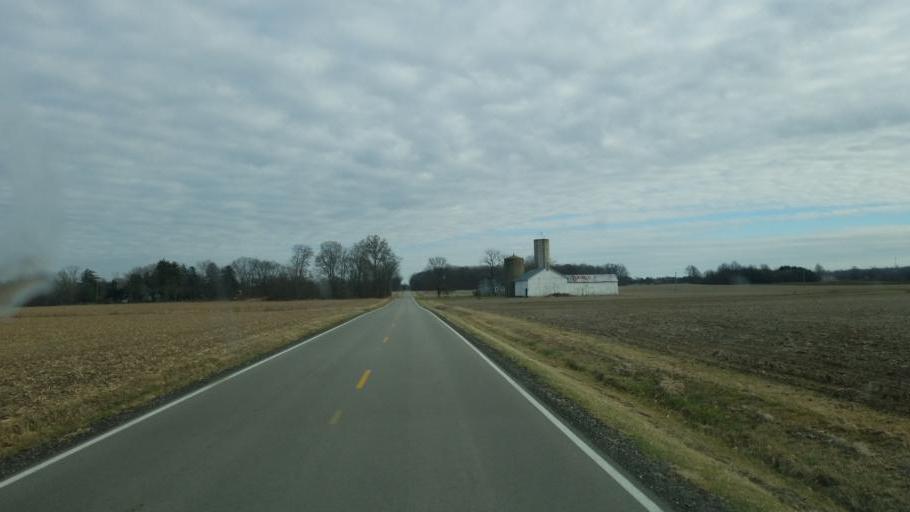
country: US
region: Ohio
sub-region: Crawford County
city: Galion
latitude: 40.7198
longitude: -82.8536
